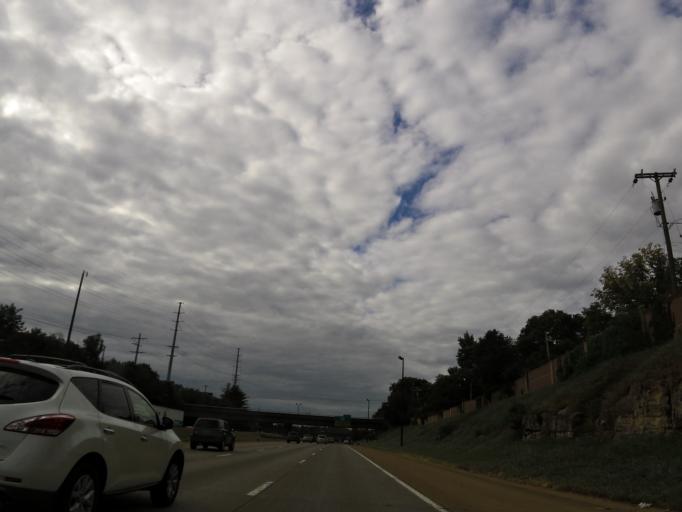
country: US
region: Tennessee
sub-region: Davidson County
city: Nashville
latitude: 36.1324
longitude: -86.8183
